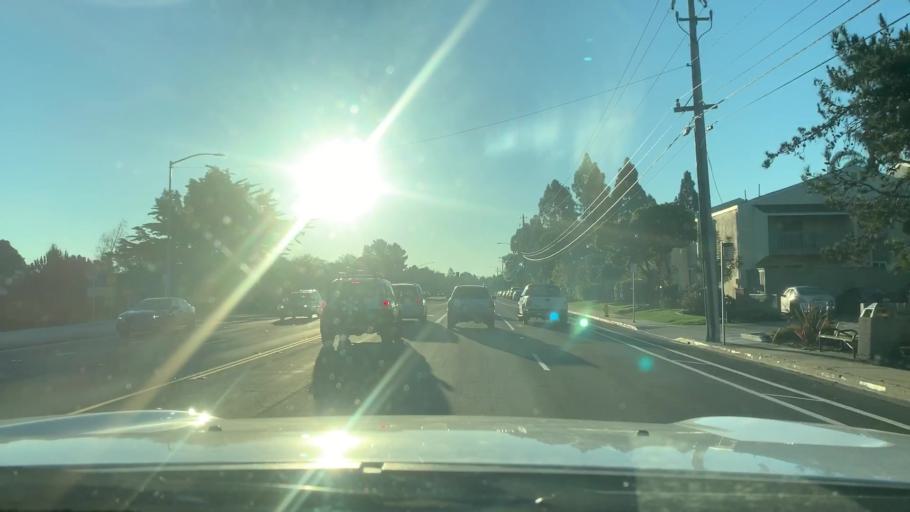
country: US
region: California
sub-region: San Luis Obispo County
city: San Luis Obispo
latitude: 35.2601
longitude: -120.6945
